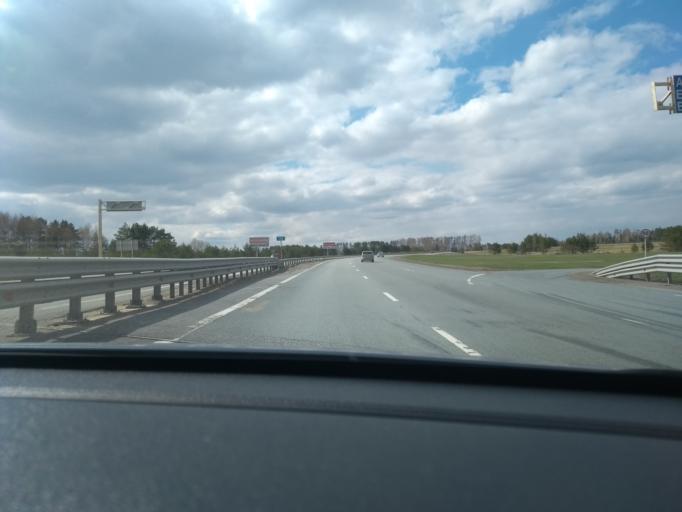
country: RU
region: Tatarstan
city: Yelabuga
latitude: 55.7823
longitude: 52.1764
